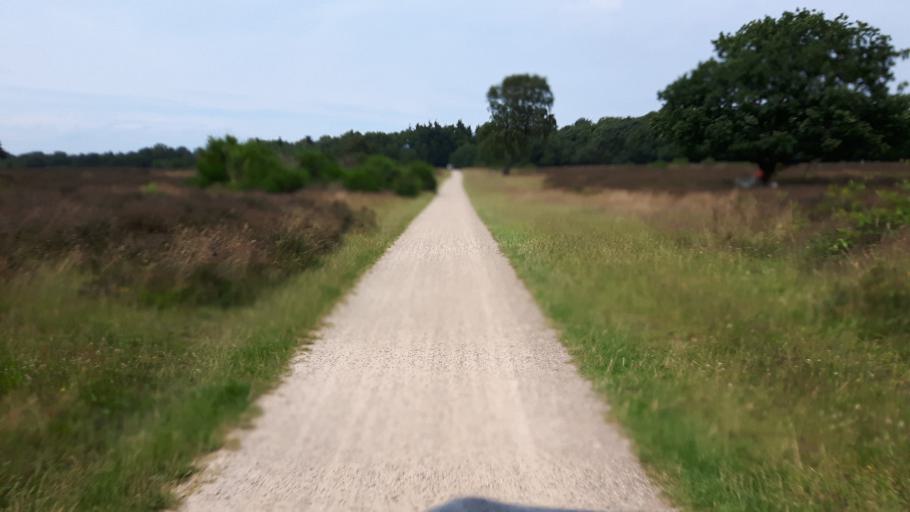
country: NL
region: North Holland
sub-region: Gemeente Hilversum
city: Hilversum
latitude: 52.2013
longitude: 5.1677
